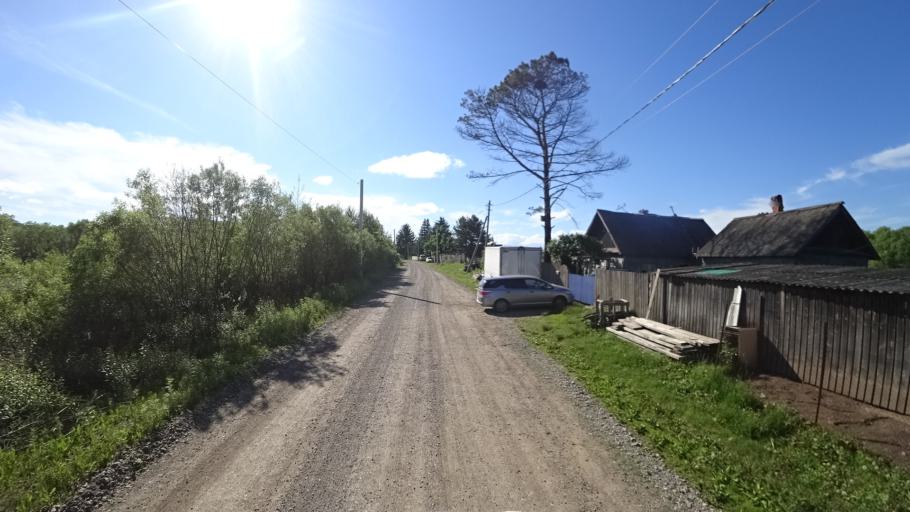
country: RU
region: Khabarovsk Krai
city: Khor
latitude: 47.8861
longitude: 135.0162
